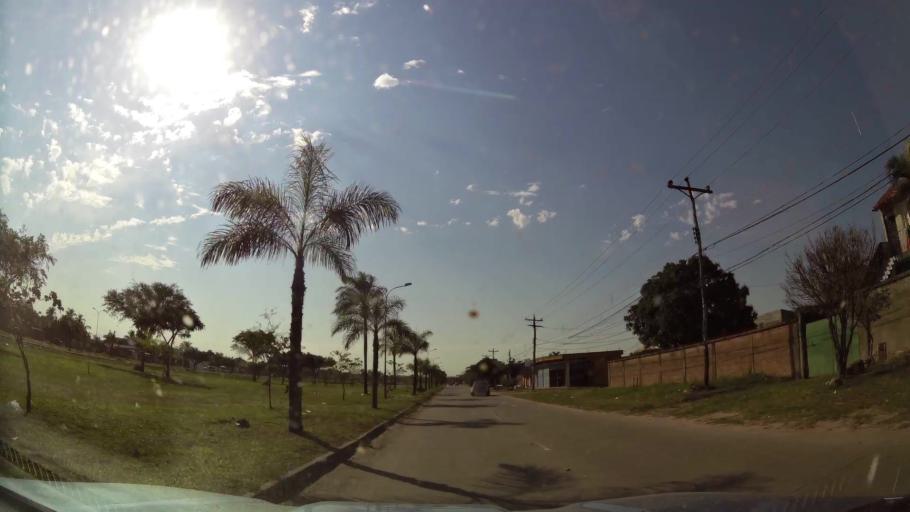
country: BO
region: Santa Cruz
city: Santa Cruz de la Sierra
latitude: -17.7968
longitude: -63.1426
